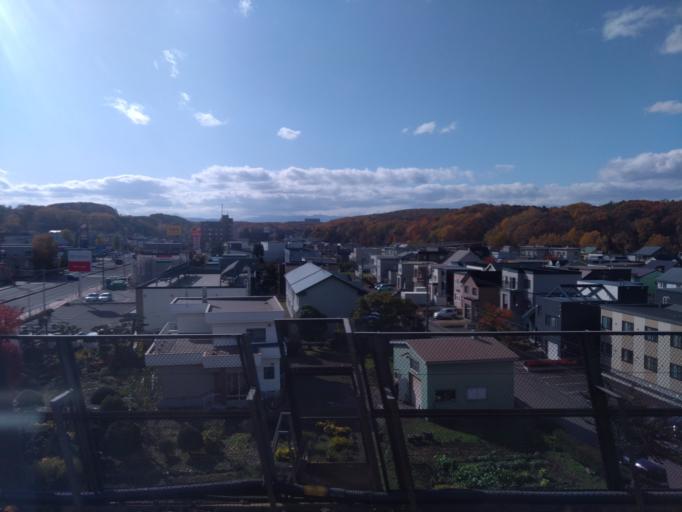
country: JP
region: Hokkaido
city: Kitahiroshima
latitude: 42.9860
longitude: 141.5617
